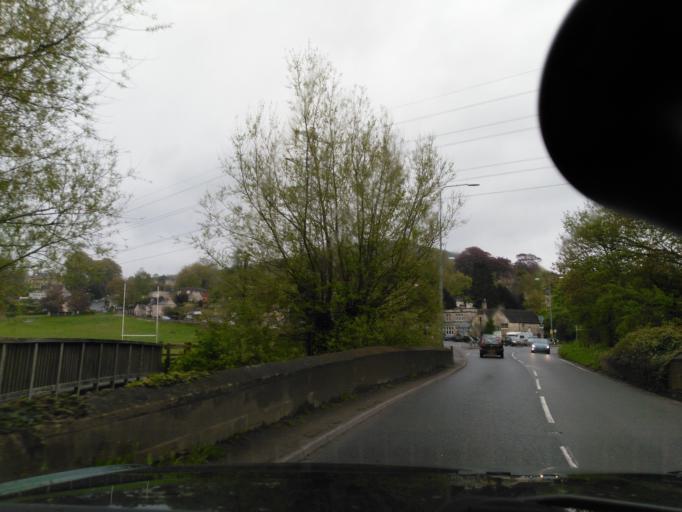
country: GB
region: England
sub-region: Wiltshire
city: Colerne
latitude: 51.4018
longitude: -2.3084
